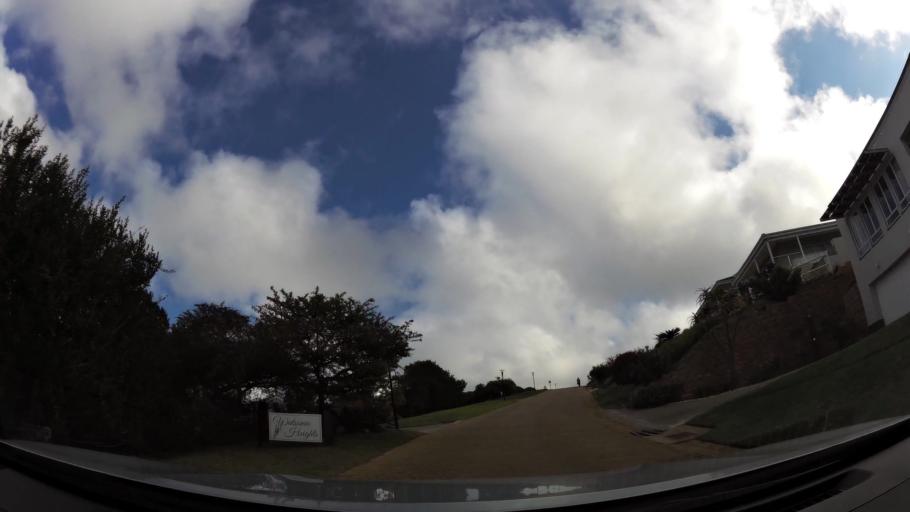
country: ZA
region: Western Cape
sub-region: Eden District Municipality
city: Plettenberg Bay
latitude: -34.0651
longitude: 23.3603
